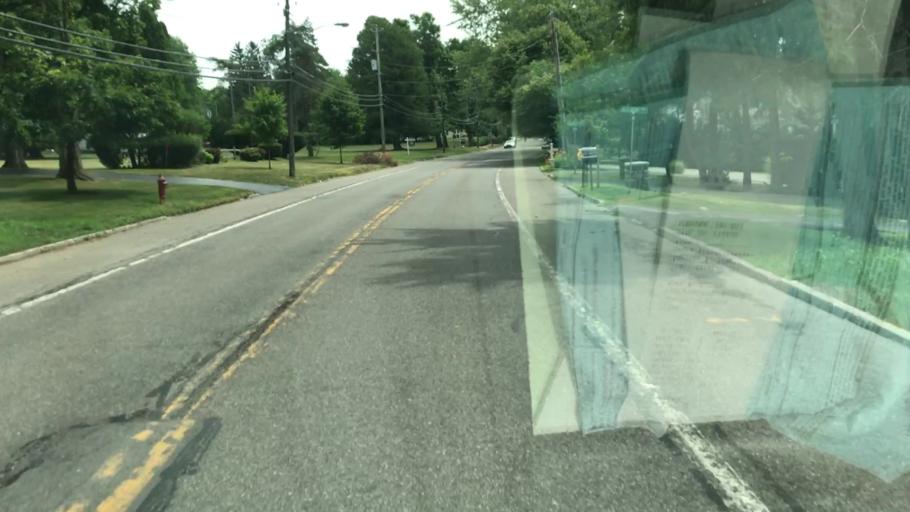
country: US
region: New York
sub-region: Onondaga County
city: Skaneateles
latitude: 42.9398
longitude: -76.4121
